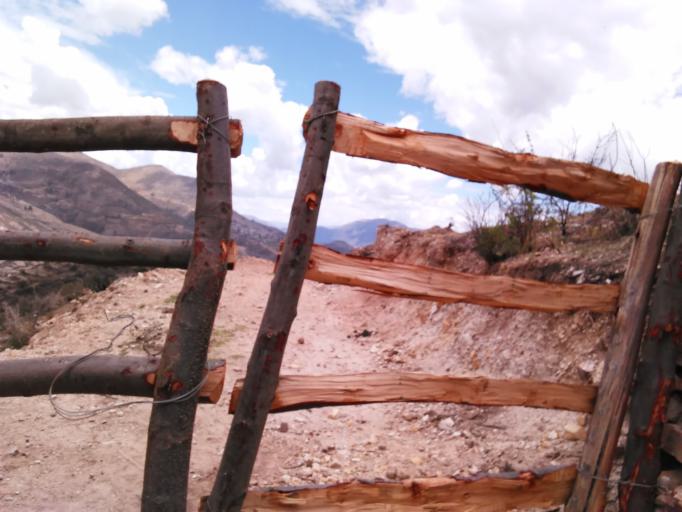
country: PE
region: Ayacucho
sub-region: Provincia de Victor Fajardo
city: Canaria
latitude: -13.8825
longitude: -73.9412
